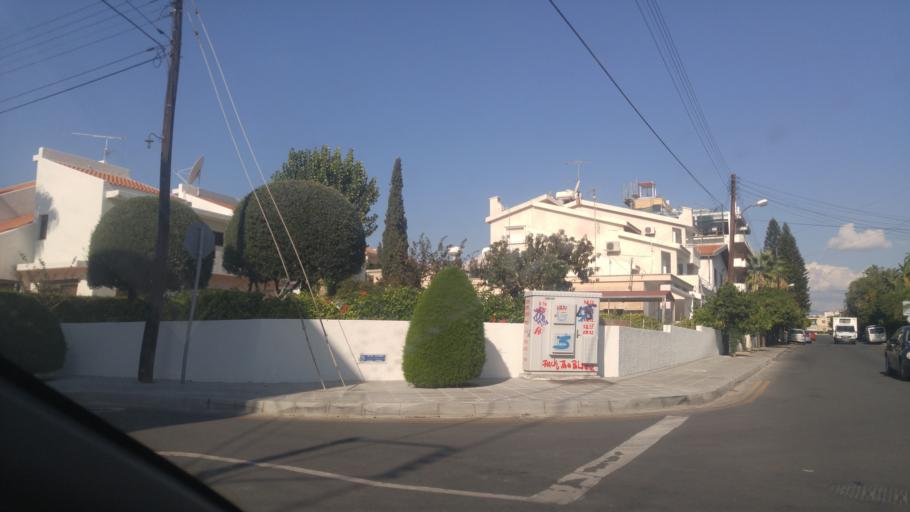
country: CY
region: Limassol
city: Limassol
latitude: 34.6913
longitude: 33.0507
